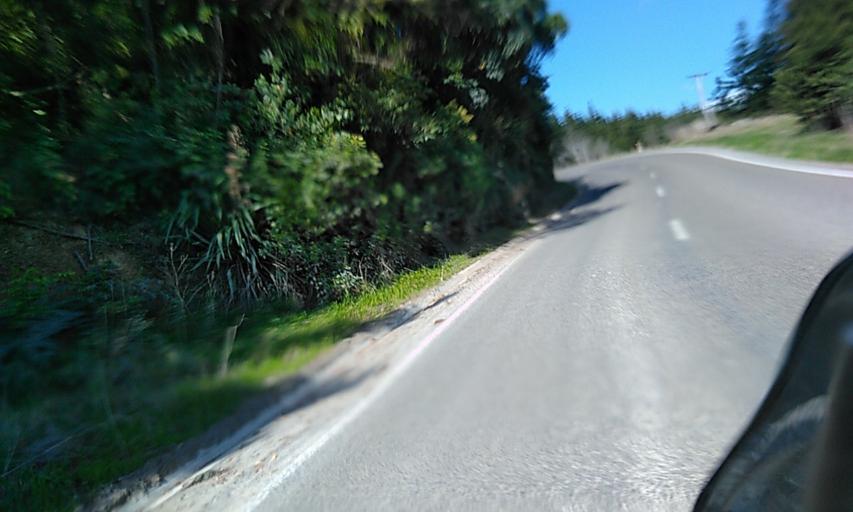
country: NZ
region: Gisborne
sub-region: Gisborne District
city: Gisborne
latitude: -38.3076
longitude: 178.1218
